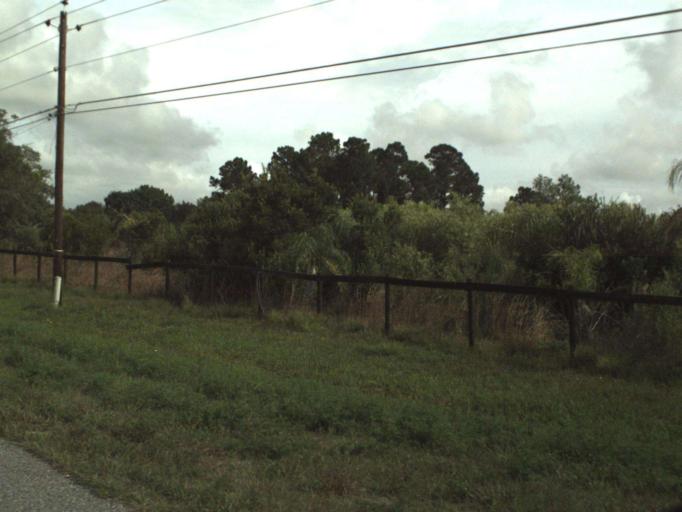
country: US
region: Florida
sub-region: Seminole County
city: Geneva
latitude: 28.7572
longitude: -81.1417
